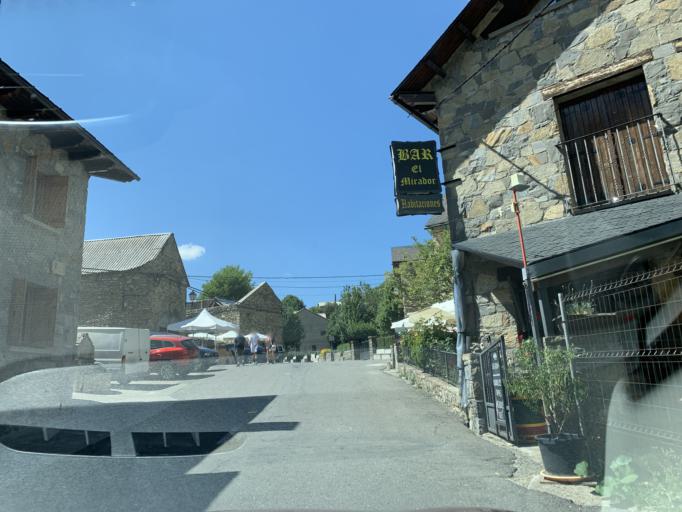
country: ES
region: Aragon
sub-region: Provincia de Huesca
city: Hoz de Jaca
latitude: 42.6902
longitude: -0.3061
